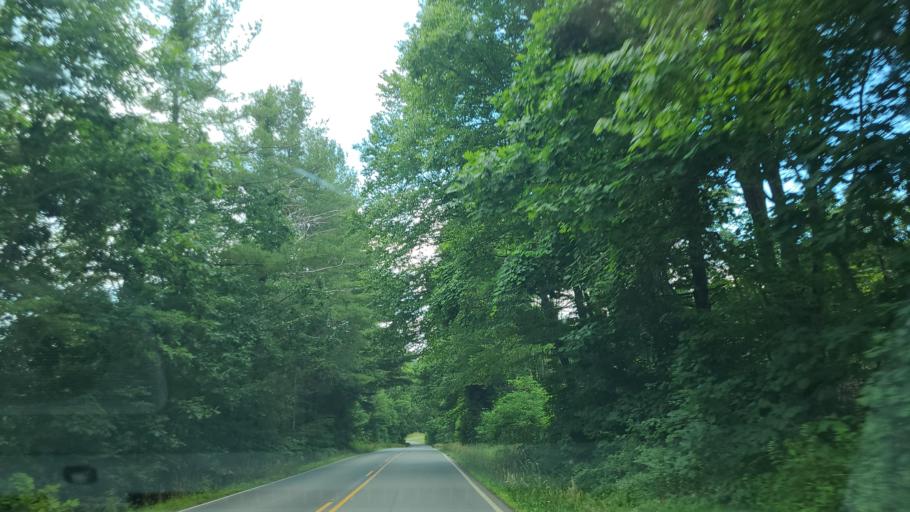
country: US
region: North Carolina
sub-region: Ashe County
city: Jefferson
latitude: 36.3930
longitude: -81.3364
